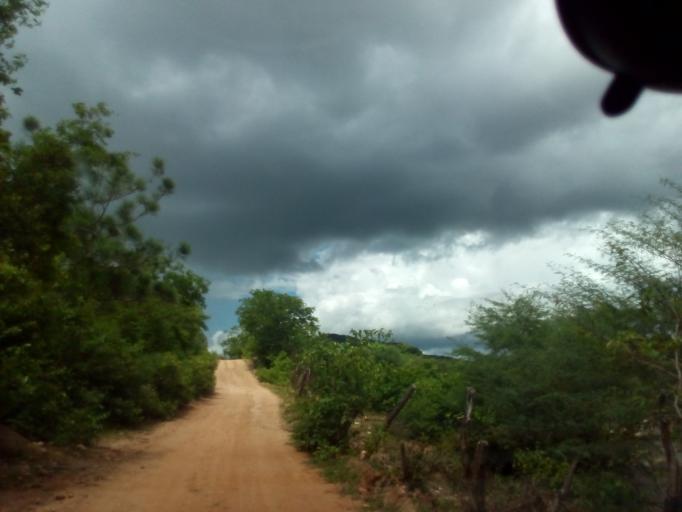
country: BR
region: Rio Grande do Norte
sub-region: Sao Tome
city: Sao Tome
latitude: -5.9520
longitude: -35.9192
